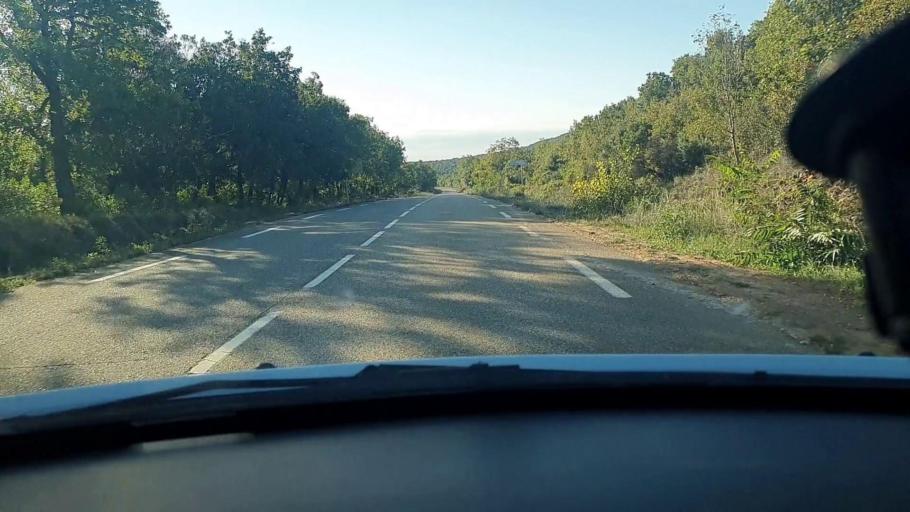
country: FR
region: Languedoc-Roussillon
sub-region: Departement du Gard
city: Barjac
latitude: 44.2213
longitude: 4.3210
